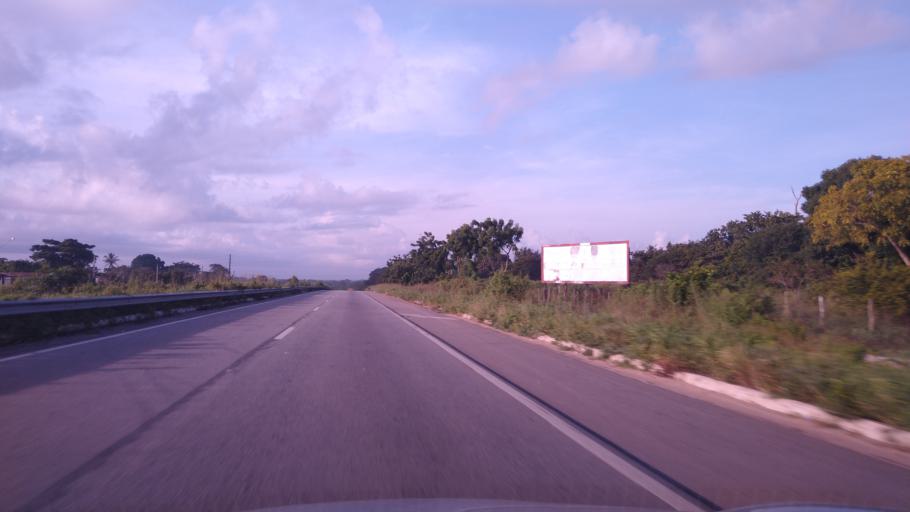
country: BR
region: Ceara
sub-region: Pacajus
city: Pacajus
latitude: -4.1750
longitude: -38.4927
